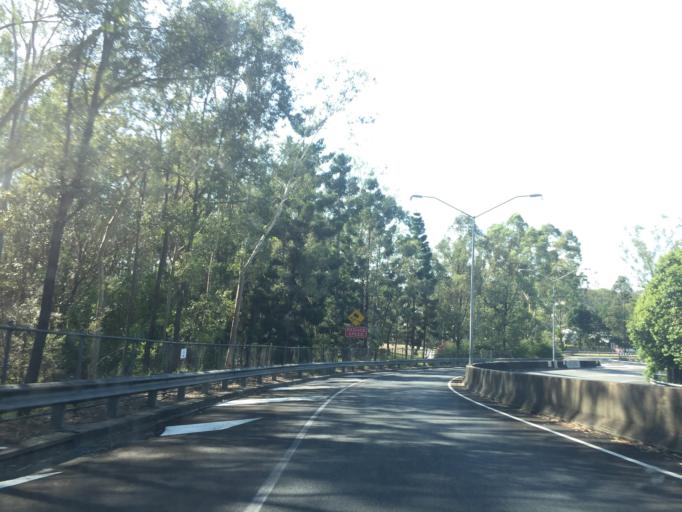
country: AU
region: Queensland
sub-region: Brisbane
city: Milton
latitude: -27.4640
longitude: 152.9887
